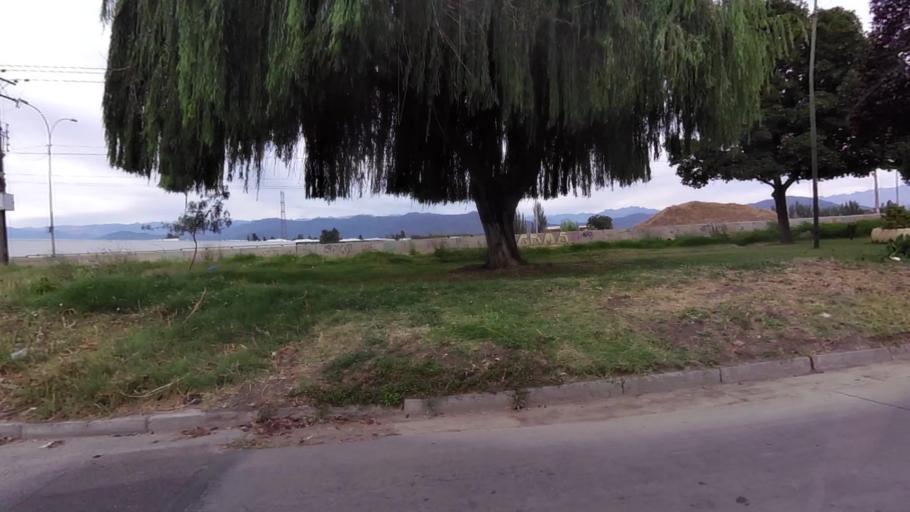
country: CL
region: O'Higgins
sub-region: Provincia de Cachapoal
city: Rancagua
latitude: -34.1487
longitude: -70.7290
